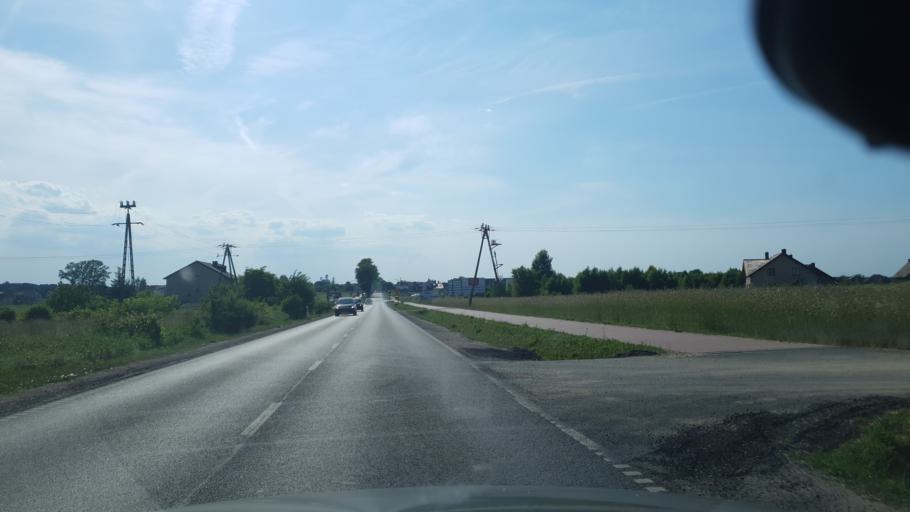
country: PL
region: Pomeranian Voivodeship
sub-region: Powiat kartuski
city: Chwaszczyno
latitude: 54.4427
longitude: 18.4347
